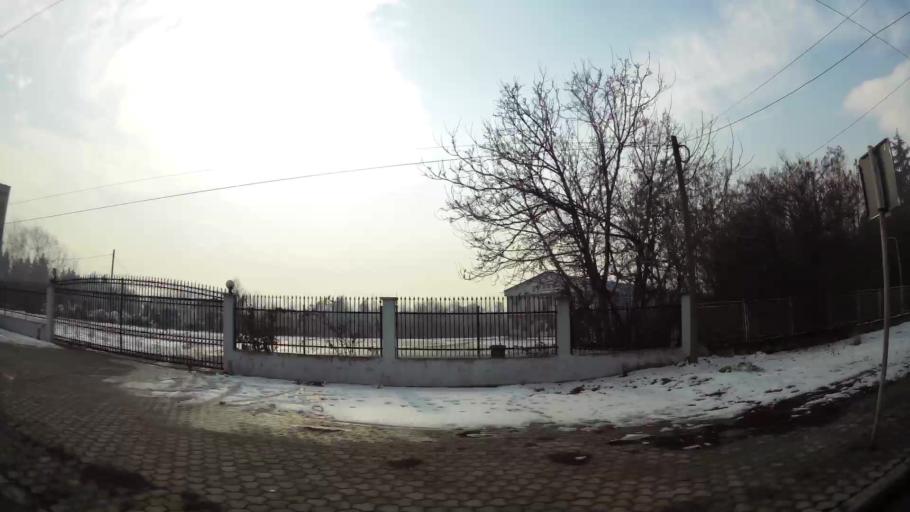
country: MK
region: Cair
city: Cair
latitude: 42.0014
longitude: 21.4839
